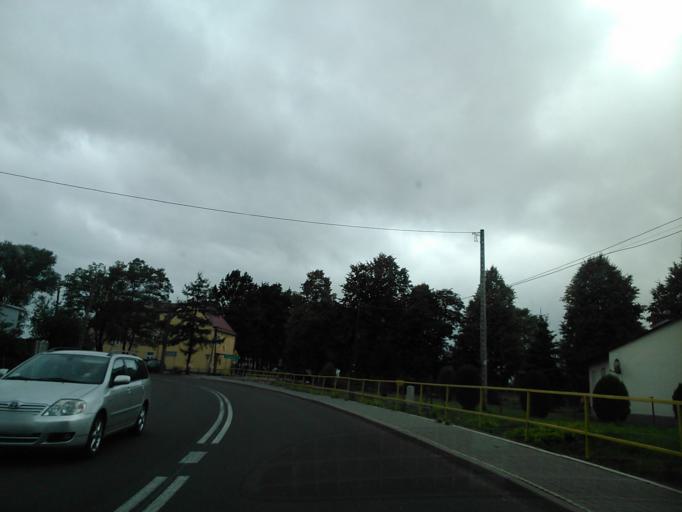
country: PL
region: Kujawsko-Pomorskie
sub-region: Powiat inowroclawski
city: Kruszwica
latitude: 52.6837
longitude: 18.2668
